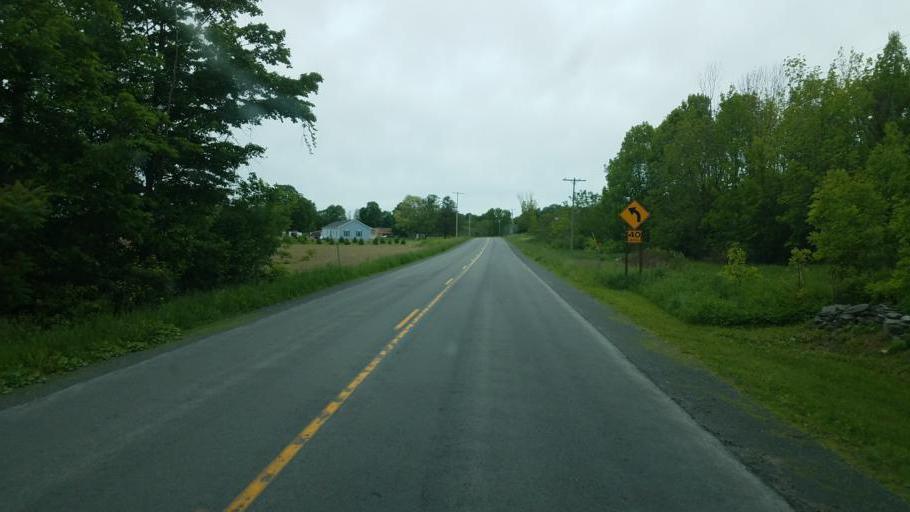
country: US
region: New York
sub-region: Oneida County
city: Chadwicks
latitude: 42.9458
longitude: -75.2219
